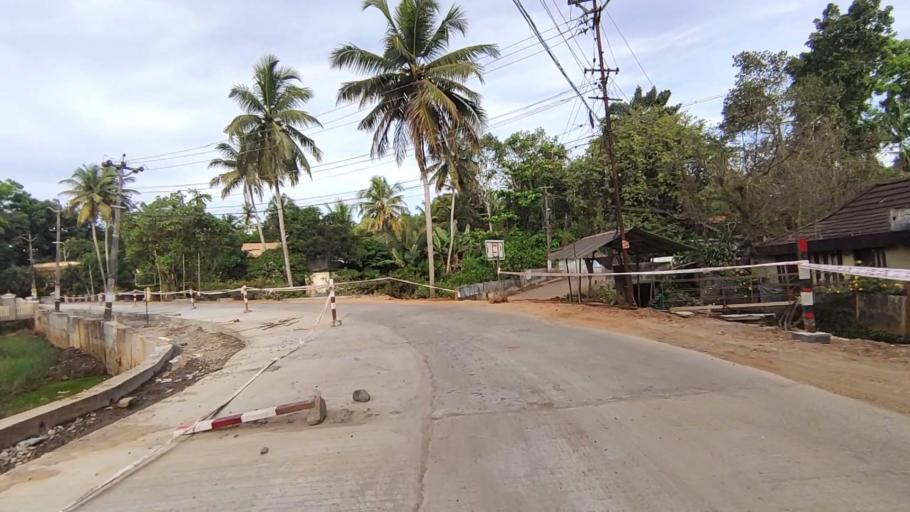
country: IN
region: Kerala
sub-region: Kottayam
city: Kottayam
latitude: 9.6082
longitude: 76.4902
